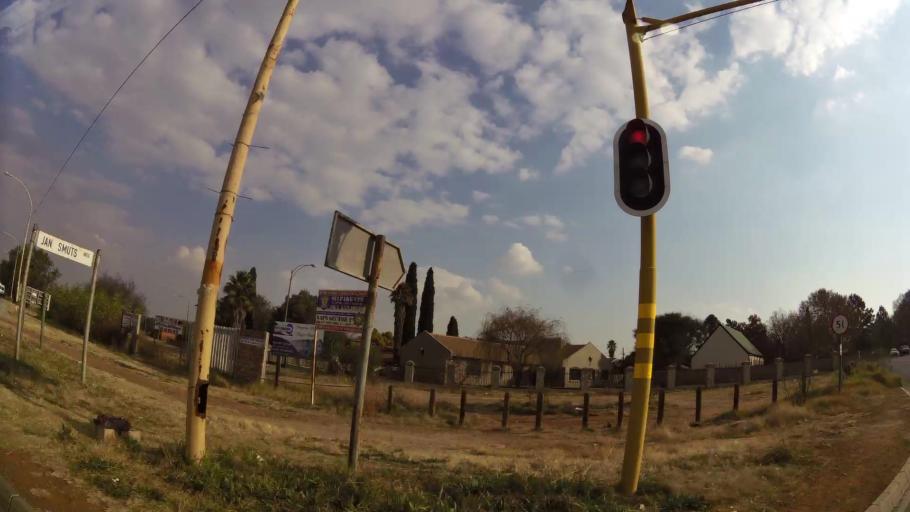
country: ZA
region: Gauteng
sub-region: Ekurhuleni Metropolitan Municipality
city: Springs
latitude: -26.2741
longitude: 28.4511
